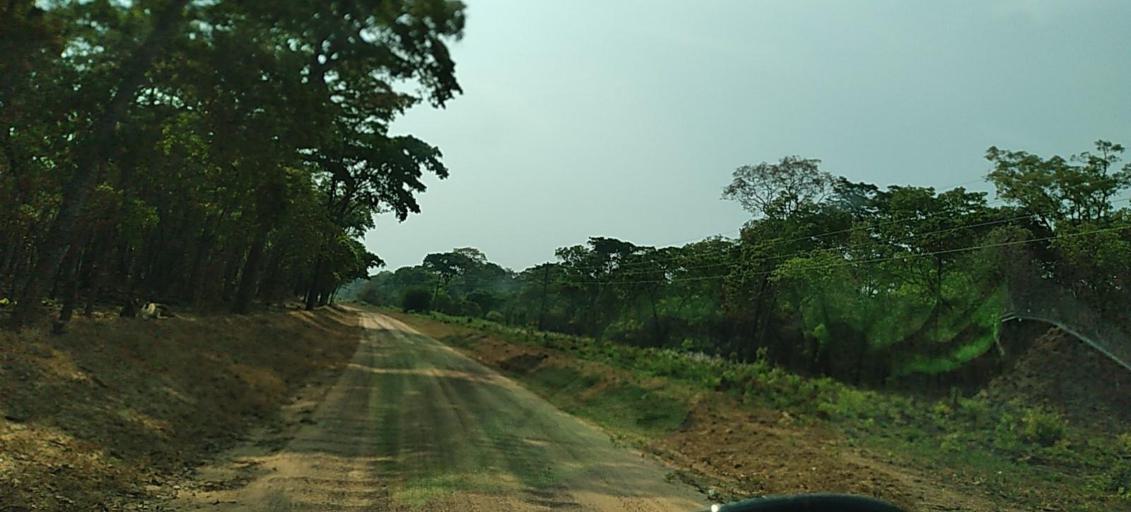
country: ZM
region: North-Western
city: Solwezi
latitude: -12.6861
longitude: 26.3951
